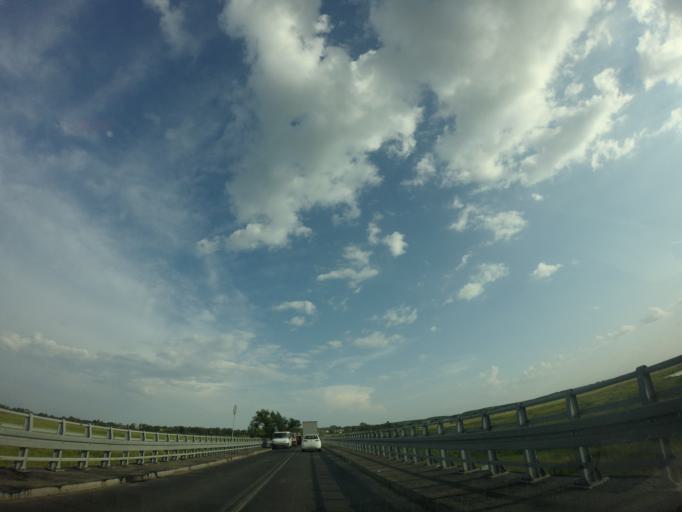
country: PL
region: Lublin Voivodeship
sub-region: Powiat lubartowski
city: Jeziorzany
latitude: 51.5987
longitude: 22.2784
